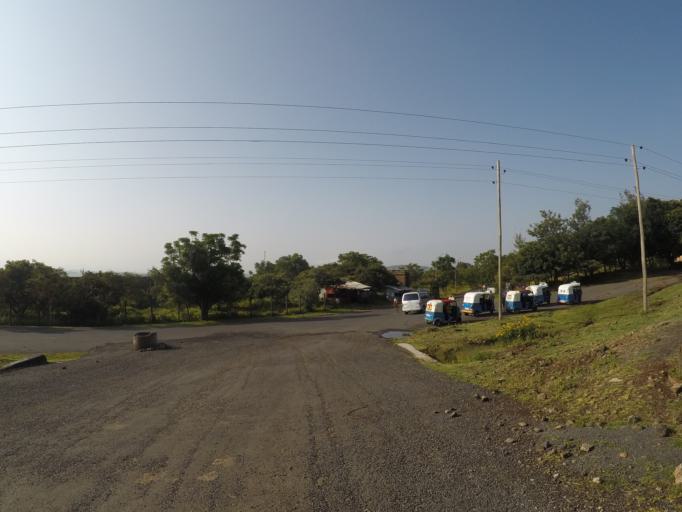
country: ET
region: Amhara
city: Gondar
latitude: 12.5210
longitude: 37.4300
